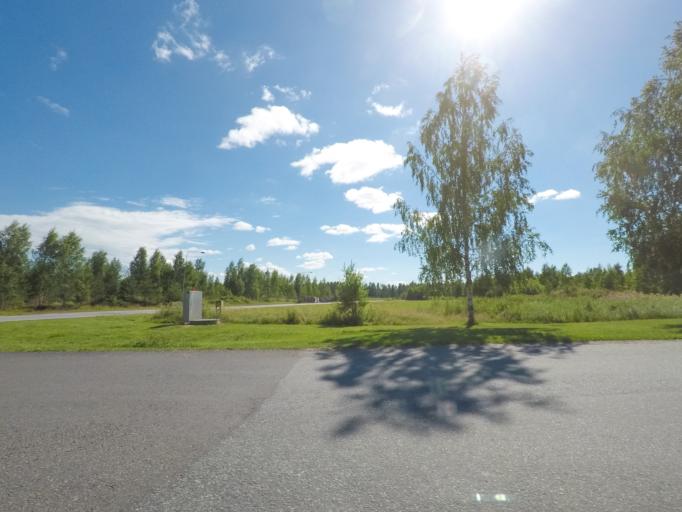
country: FI
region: Southern Savonia
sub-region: Pieksaemaeki
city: Juva
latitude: 61.8964
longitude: 27.8076
